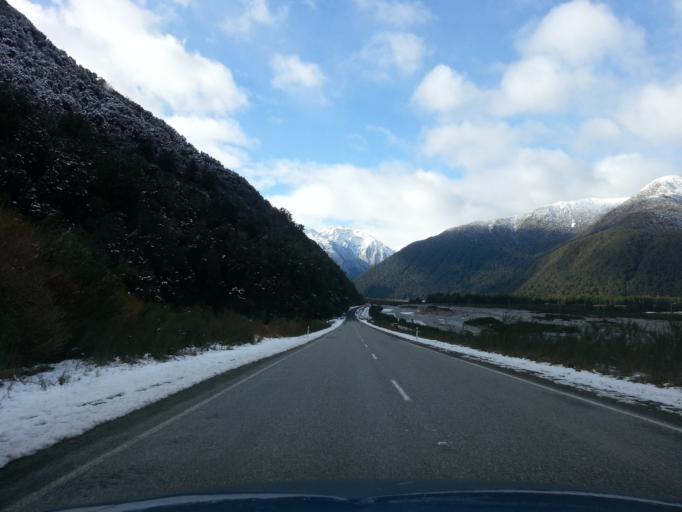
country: NZ
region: West Coast
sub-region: Grey District
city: Greymouth
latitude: -42.7948
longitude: 171.5895
